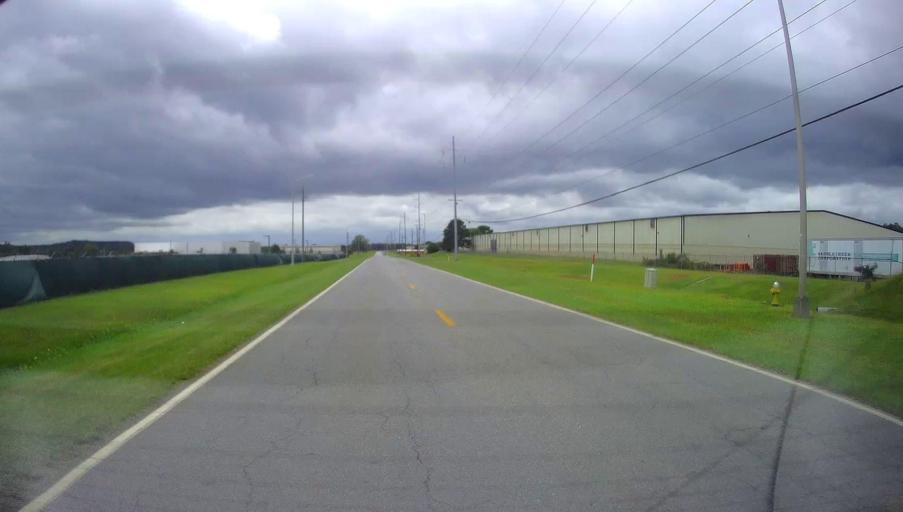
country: US
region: Georgia
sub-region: Bibb County
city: Macon
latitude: 32.8070
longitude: -83.5488
